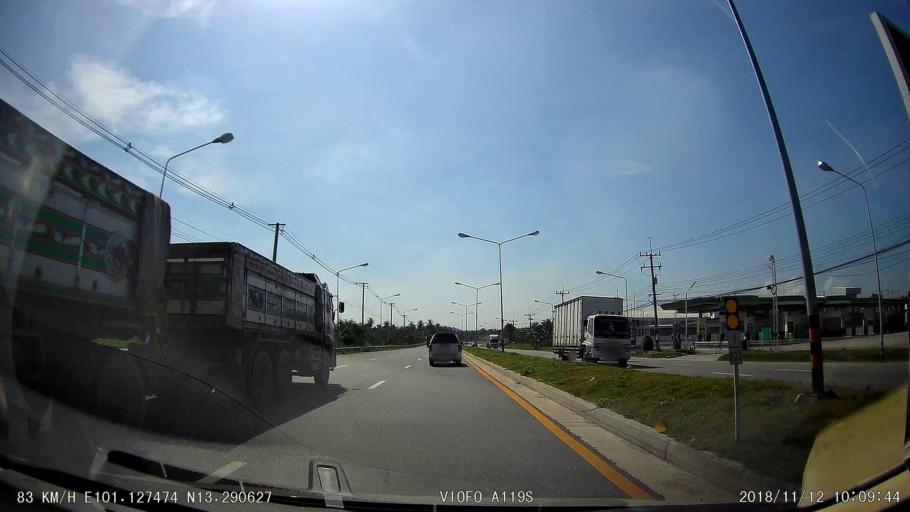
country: TH
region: Chon Buri
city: Ban Bueng
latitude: 13.2904
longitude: 101.1276
